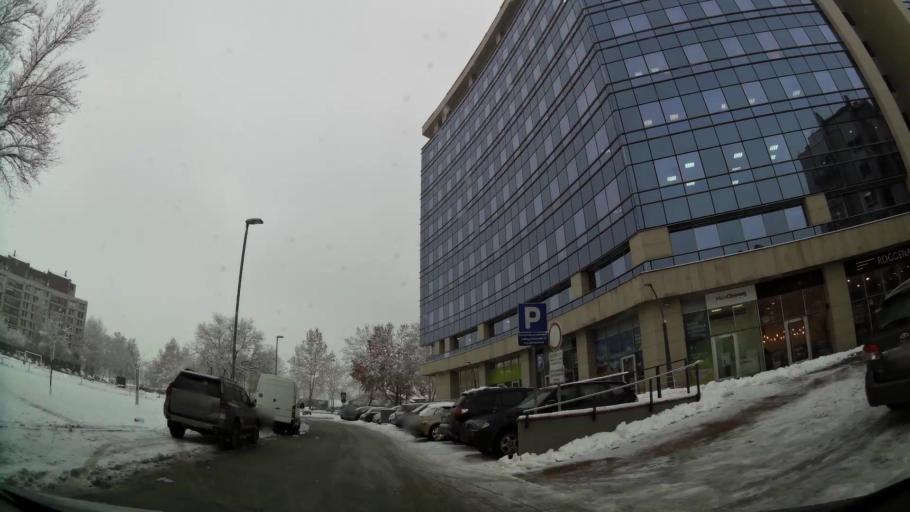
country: RS
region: Central Serbia
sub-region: Belgrade
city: Novi Beograd
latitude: 44.8047
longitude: 20.4283
